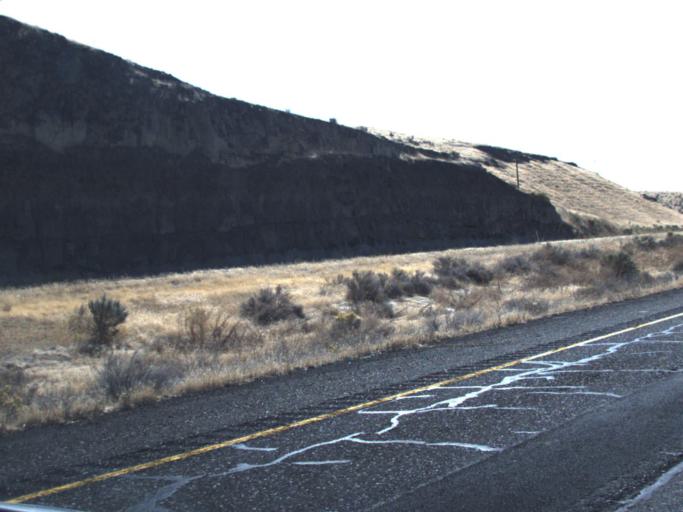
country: US
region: Washington
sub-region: Franklin County
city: Basin City
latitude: 46.4781
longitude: -119.0111
